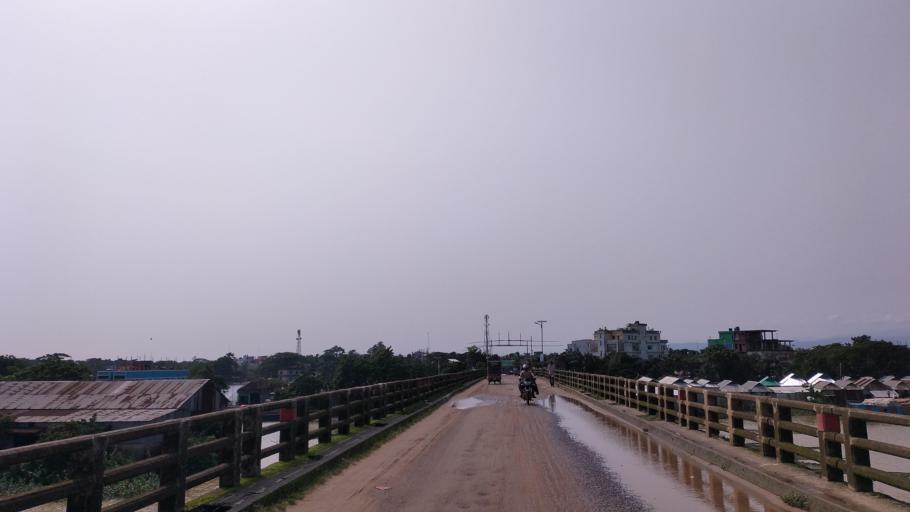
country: BD
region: Dhaka
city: Netrakona
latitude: 25.0748
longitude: 90.8907
